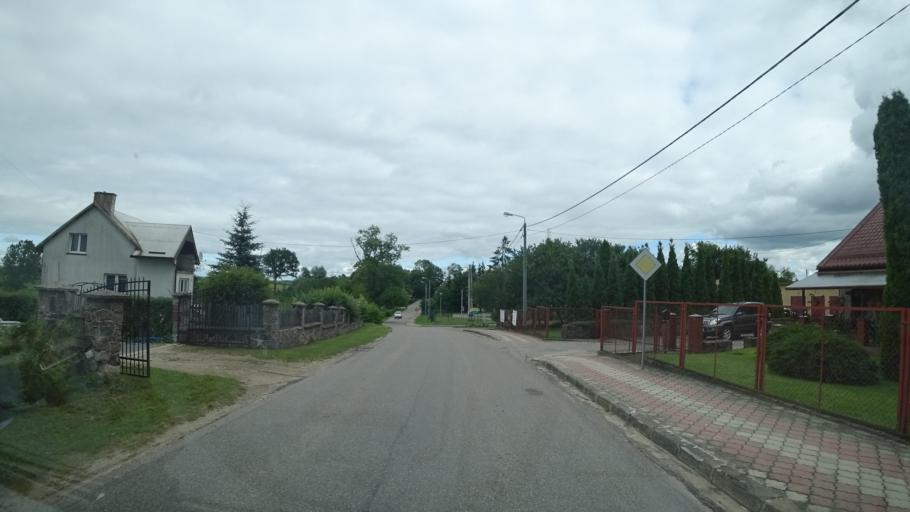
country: PL
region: Podlasie
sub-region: Powiat suwalski
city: Filipow
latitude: 54.2886
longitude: 22.5610
